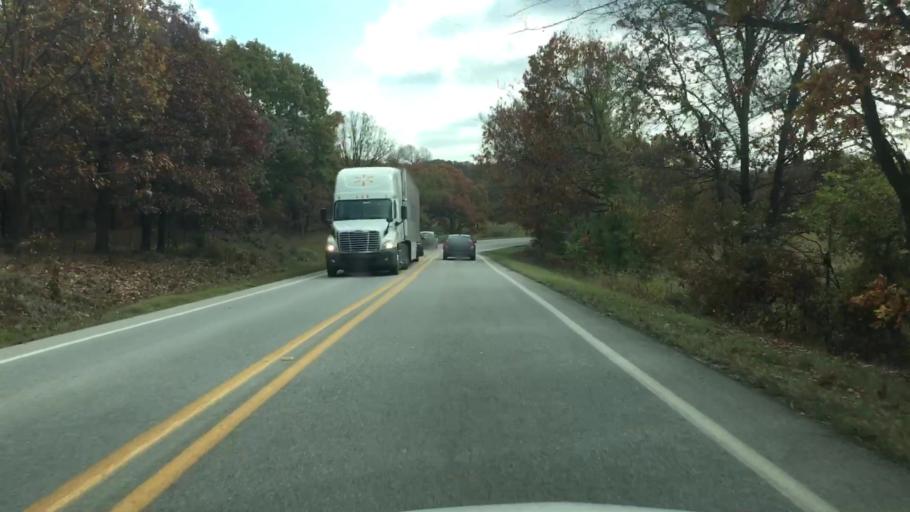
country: US
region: Arkansas
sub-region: Benton County
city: Gentry
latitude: 36.2624
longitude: -94.4511
